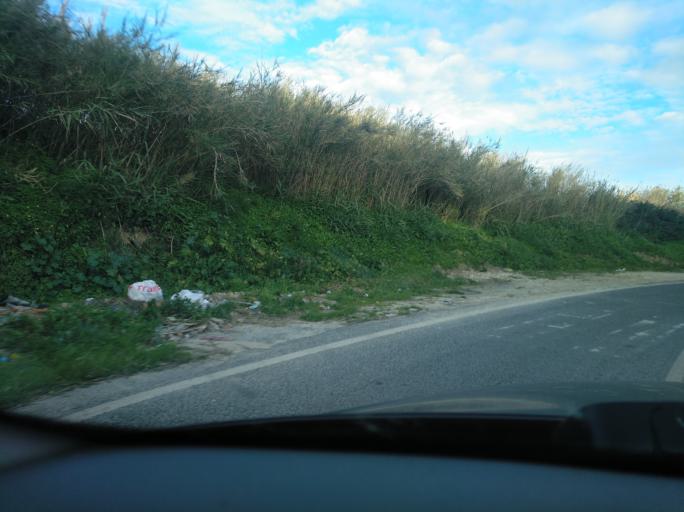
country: PT
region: Lisbon
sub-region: Loures
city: Unhos
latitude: 38.8231
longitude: -9.1261
